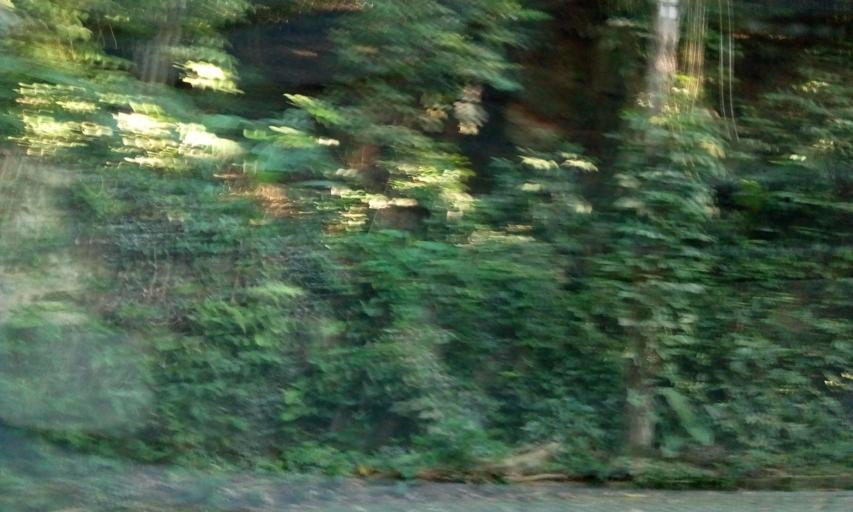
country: BR
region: Rio de Janeiro
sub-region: Rio De Janeiro
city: Rio de Janeiro
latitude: -22.9542
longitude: -43.2020
